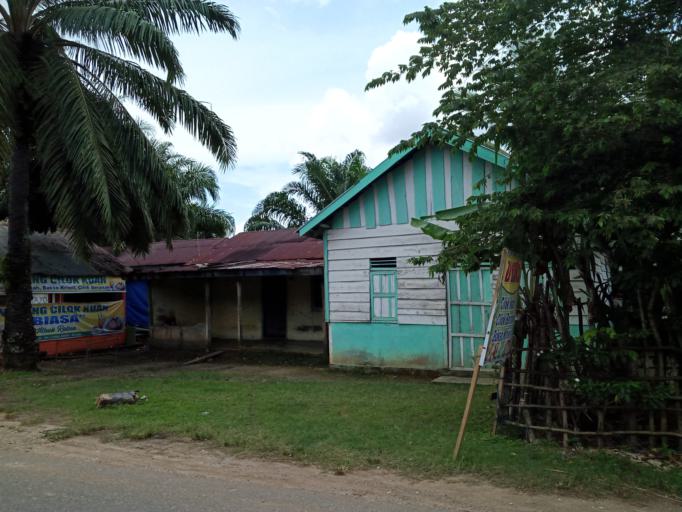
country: ID
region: Jambi
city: Mersam
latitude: -1.6467
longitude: 102.9687
